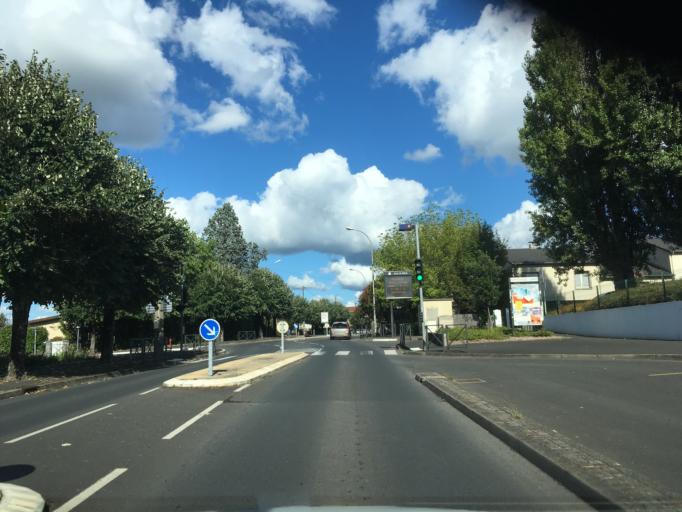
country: FR
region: Limousin
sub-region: Departement de la Correze
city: Brive-la-Gaillarde
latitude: 45.1430
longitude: 1.4920
